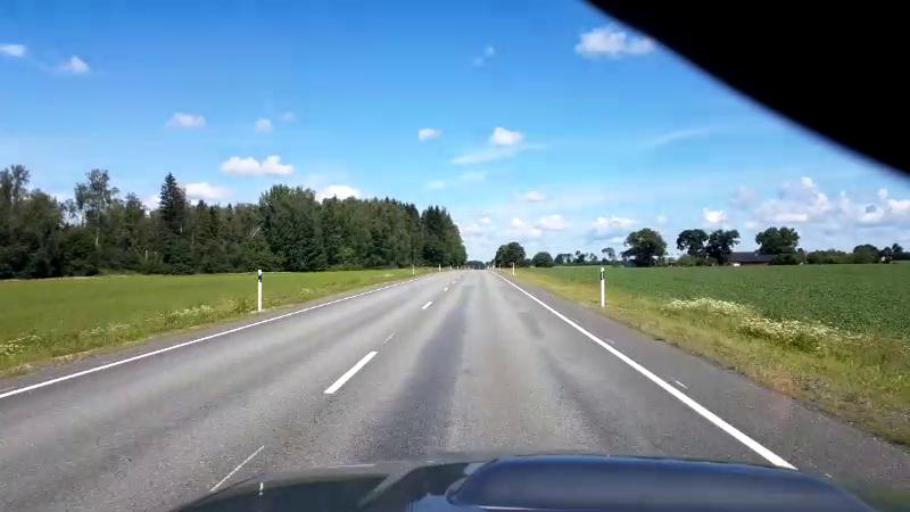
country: EE
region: Jaervamaa
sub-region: Jaerva-Jaani vald
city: Jarva-Jaani
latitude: 59.1626
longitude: 25.7614
